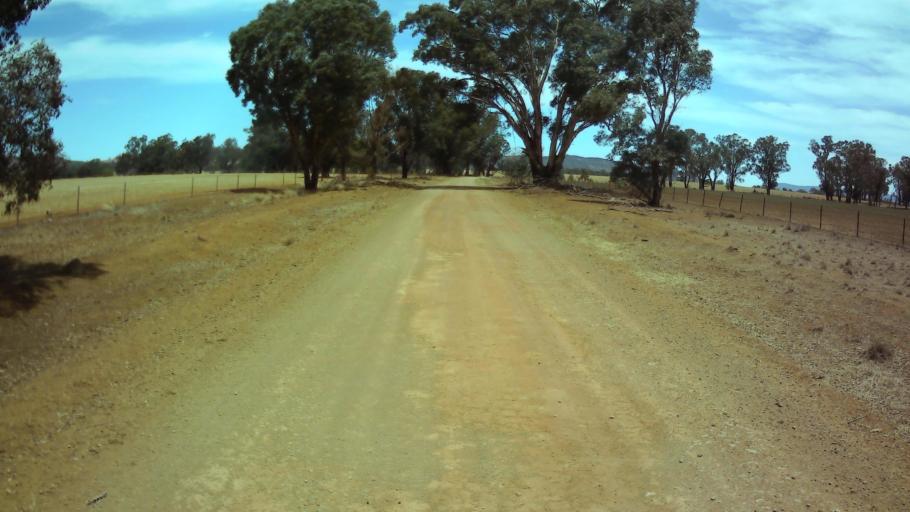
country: AU
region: New South Wales
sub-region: Weddin
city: Grenfell
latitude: -33.7557
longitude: 148.1435
